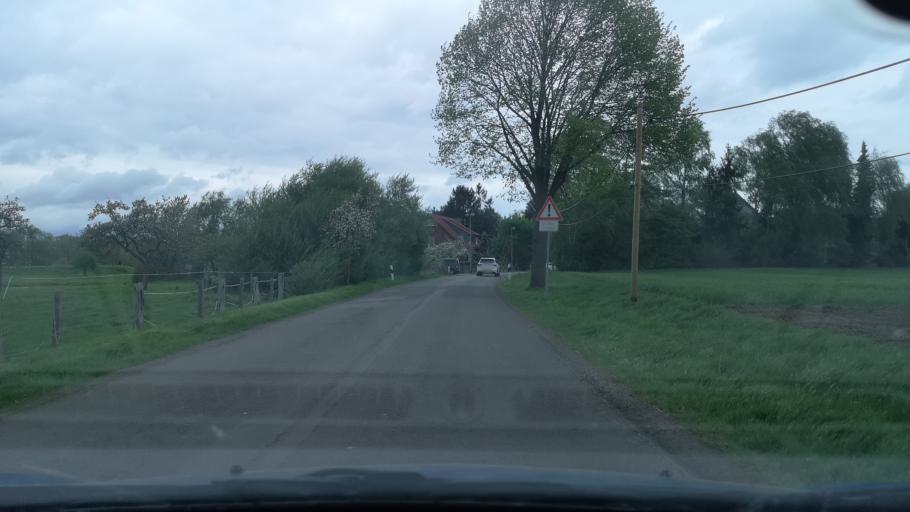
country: DE
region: Lower Saxony
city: Langenhagen
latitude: 52.4866
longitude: 9.7391
